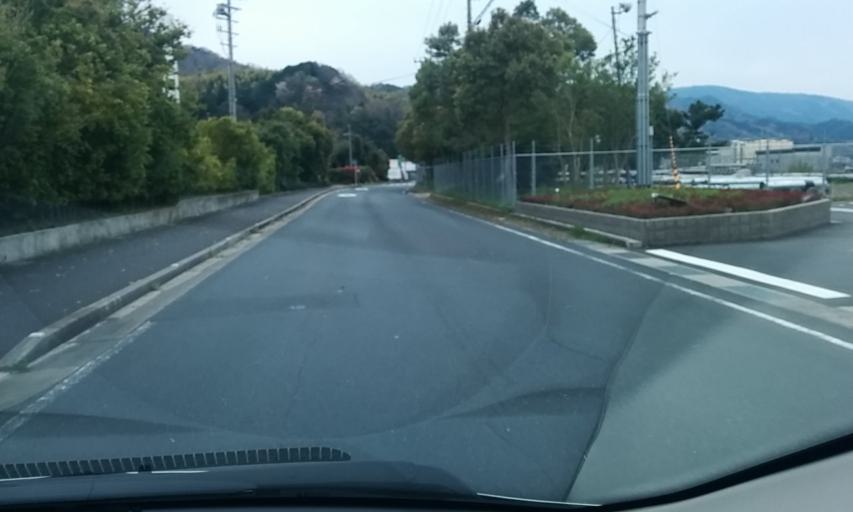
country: JP
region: Kyoto
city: Miyazu
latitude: 35.5505
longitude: 135.2111
